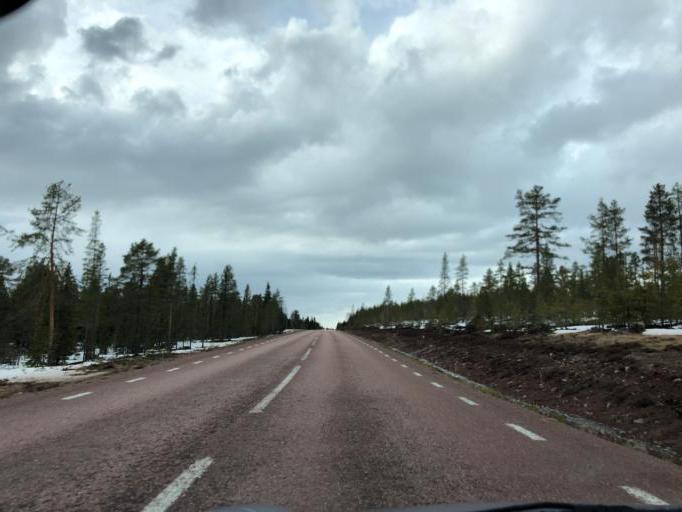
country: SE
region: Dalarna
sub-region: Alvdalens Kommun
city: AElvdalen
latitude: 61.4145
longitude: 13.4847
